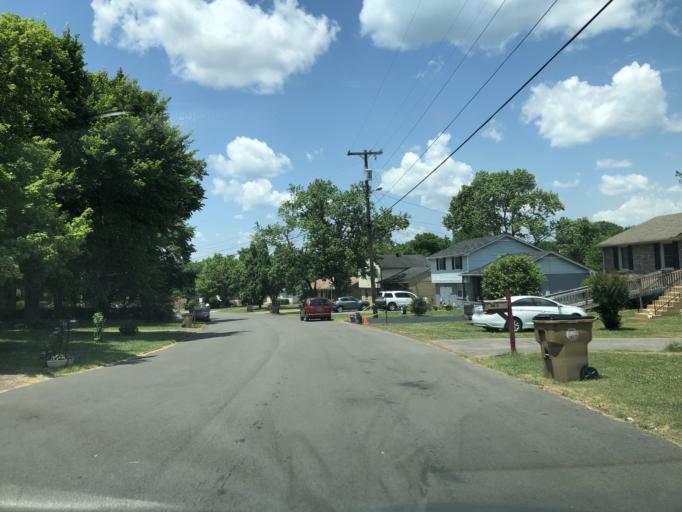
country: US
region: Tennessee
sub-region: Davidson County
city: Goodlettsville
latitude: 36.2712
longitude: -86.6991
